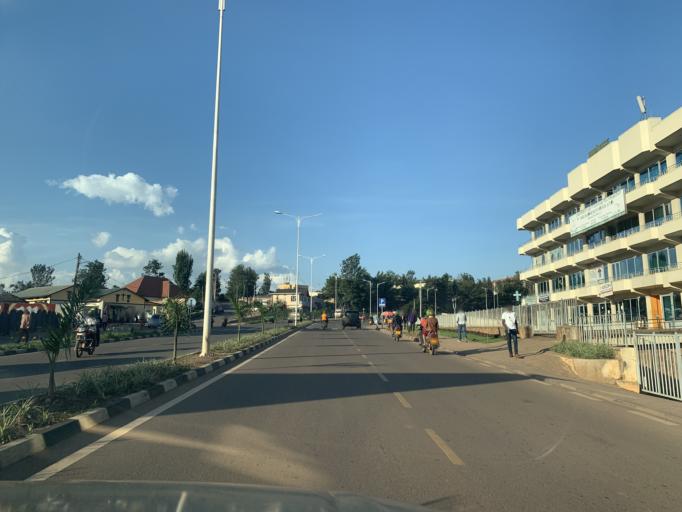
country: RW
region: Kigali
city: Kigali
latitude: -1.9666
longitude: 30.1030
